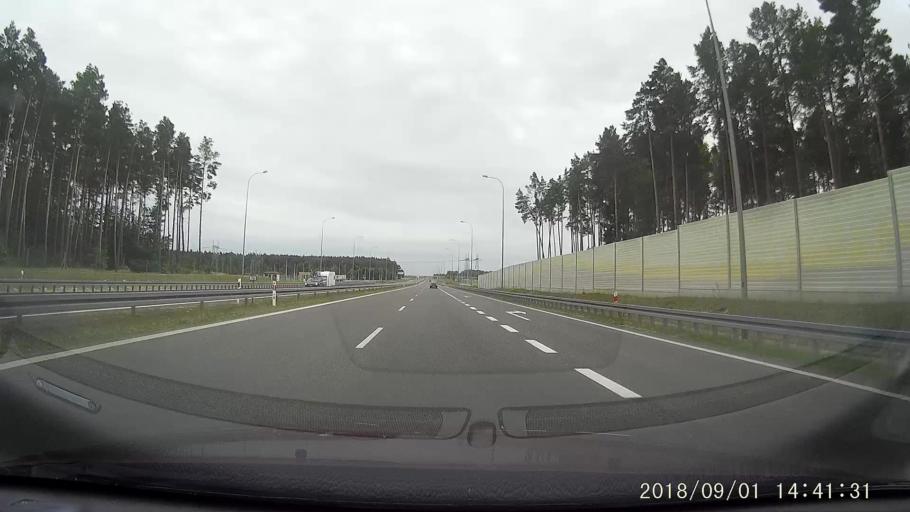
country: PL
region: Lubusz
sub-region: Powiat gorzowski
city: Jenin
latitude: 52.7904
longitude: 15.1167
